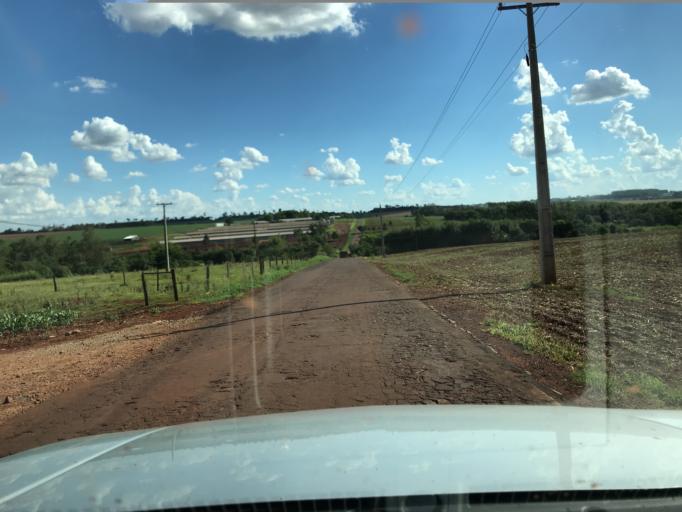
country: BR
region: Parana
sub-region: Palotina
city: Palotina
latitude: -24.2543
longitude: -53.7960
